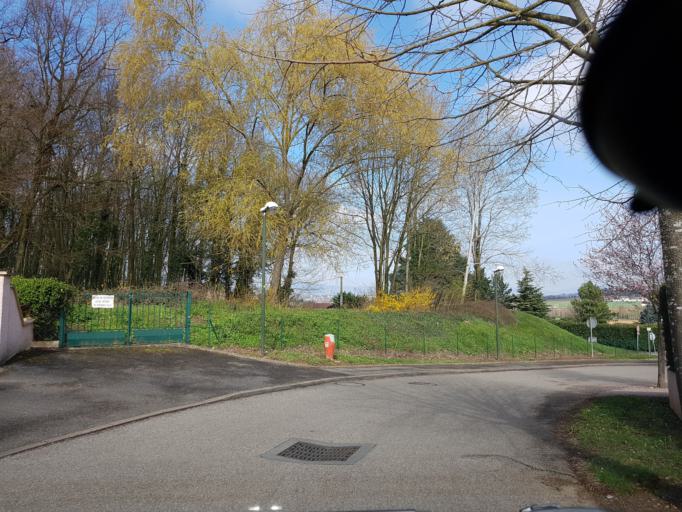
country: FR
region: Rhone-Alpes
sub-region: Departement de l'Ain
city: Trevoux
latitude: 45.9490
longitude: 4.7618
